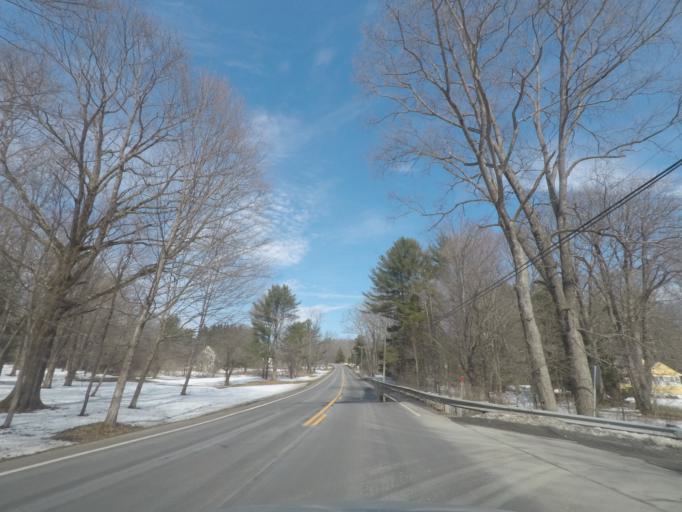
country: US
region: Massachusetts
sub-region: Berkshire County
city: West Stockbridge
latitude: 42.3544
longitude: -73.3821
